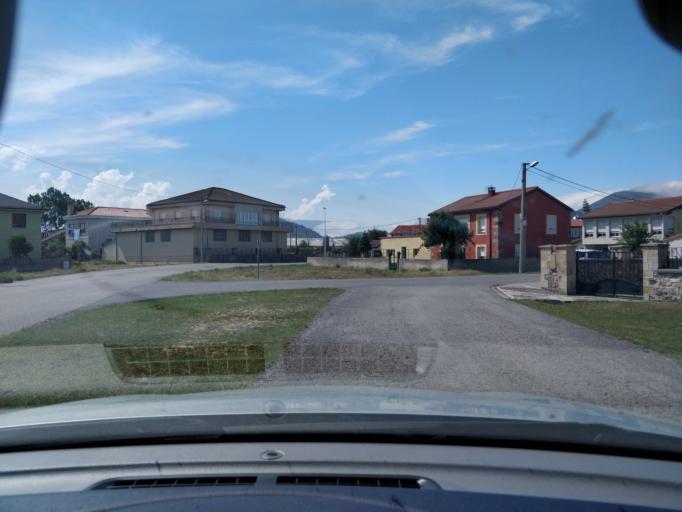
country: ES
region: Cantabria
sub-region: Provincia de Cantabria
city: Reinosa
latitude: 42.9975
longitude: -4.1560
